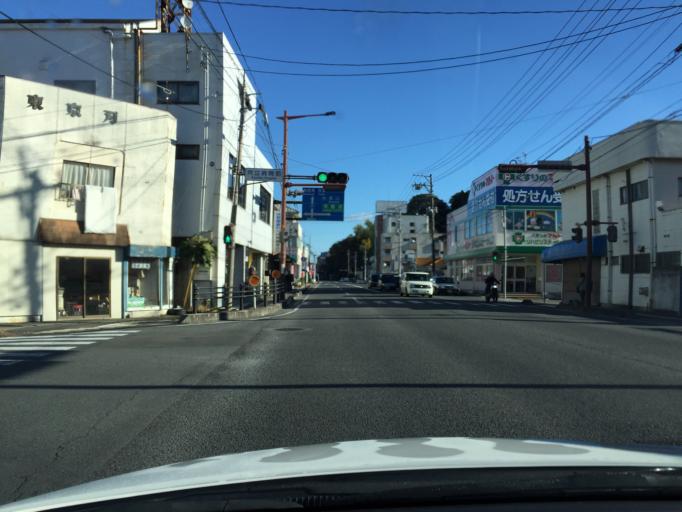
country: JP
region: Fukushima
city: Iwaki
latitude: 37.0423
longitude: 140.8667
